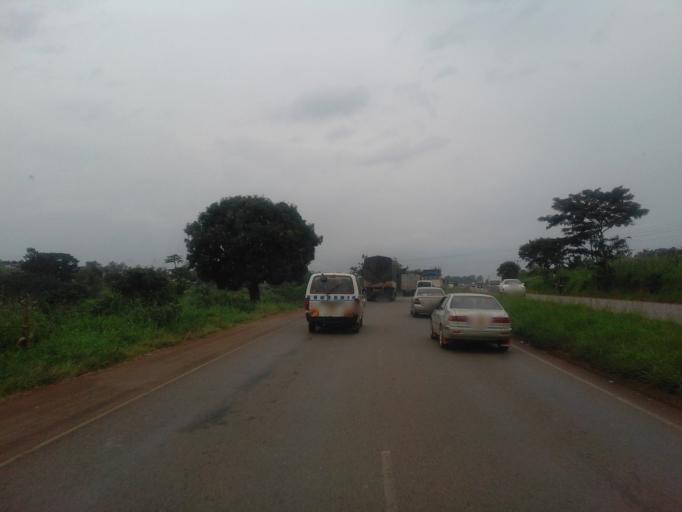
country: UG
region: Eastern Region
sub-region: Jinja District
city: Jinja
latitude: 0.4459
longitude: 33.2034
